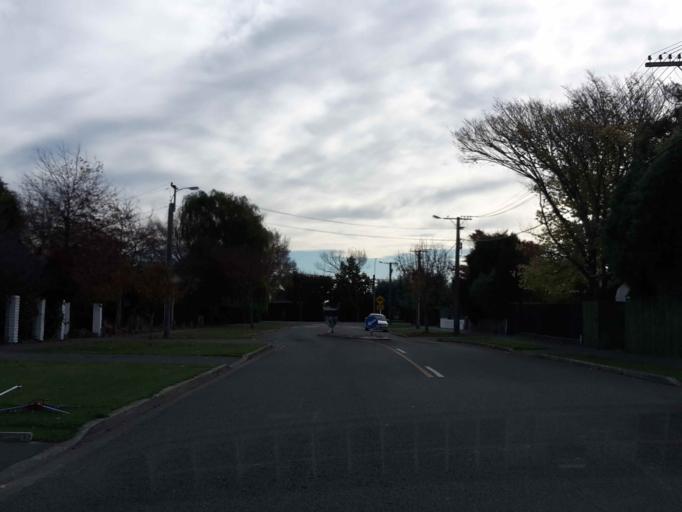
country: NZ
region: Canterbury
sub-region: Christchurch City
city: Christchurch
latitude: -43.5672
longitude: 172.6209
